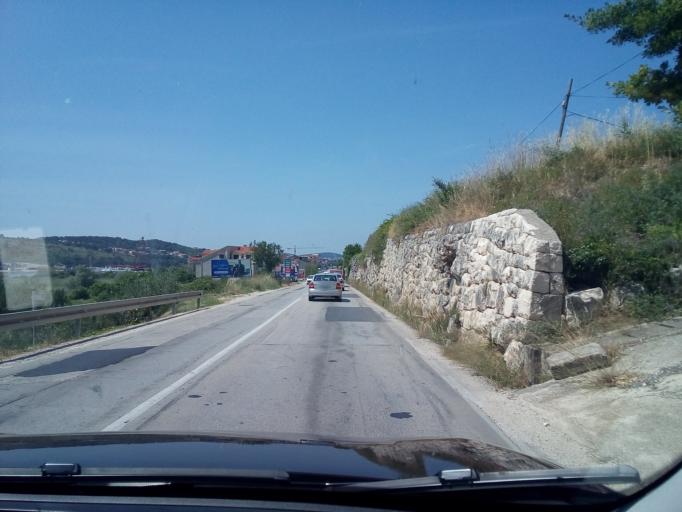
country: HR
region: Splitsko-Dalmatinska
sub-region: Grad Trogir
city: Trogir
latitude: 43.5270
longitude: 16.2715
